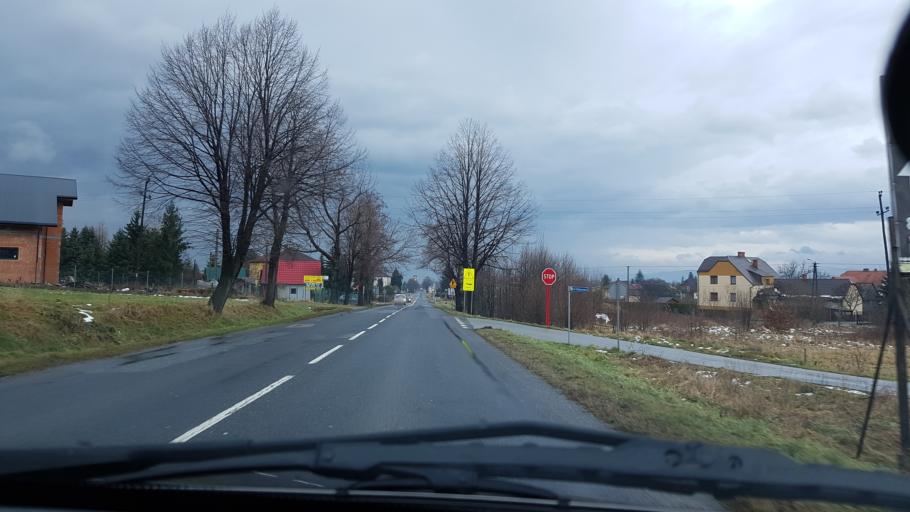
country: PL
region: Silesian Voivodeship
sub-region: Powiat bielski
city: Rybarzowice
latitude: 49.7328
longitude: 19.1192
